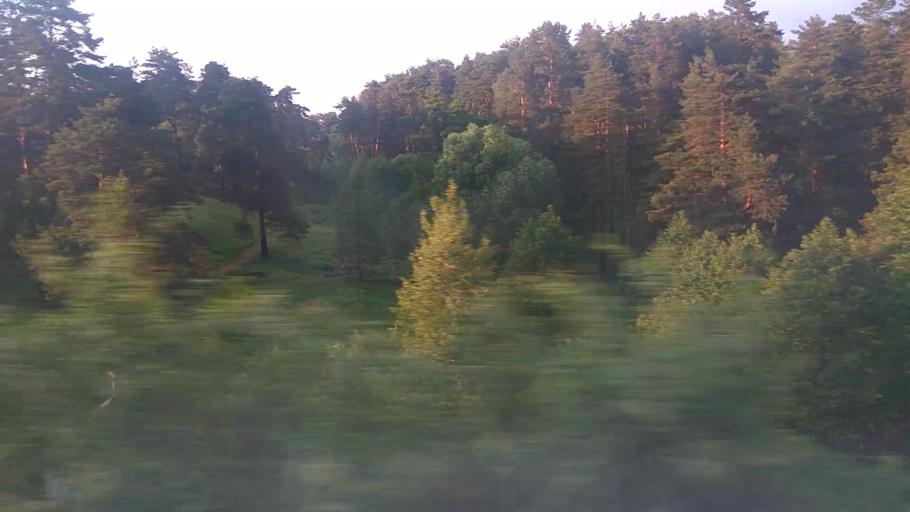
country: RU
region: Moskovskaya
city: Stupino
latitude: 54.8757
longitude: 38.1151
